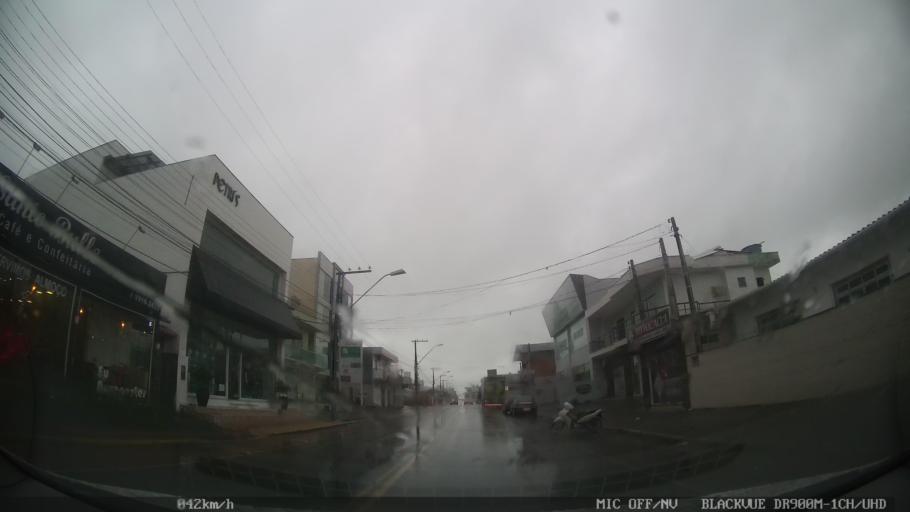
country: BR
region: Santa Catarina
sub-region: Navegantes
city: Navegantes
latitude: -26.8960
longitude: -48.6514
